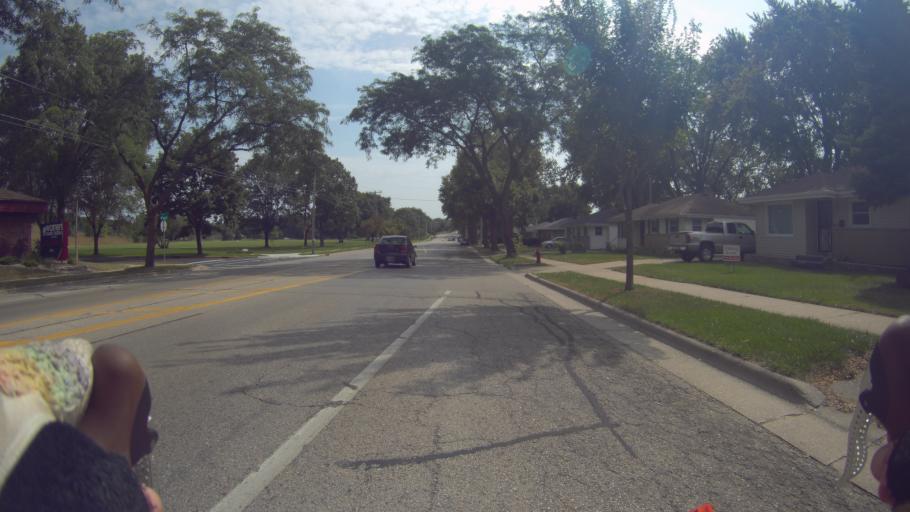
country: US
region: Wisconsin
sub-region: Dane County
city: Monona
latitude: 43.0985
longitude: -89.3108
